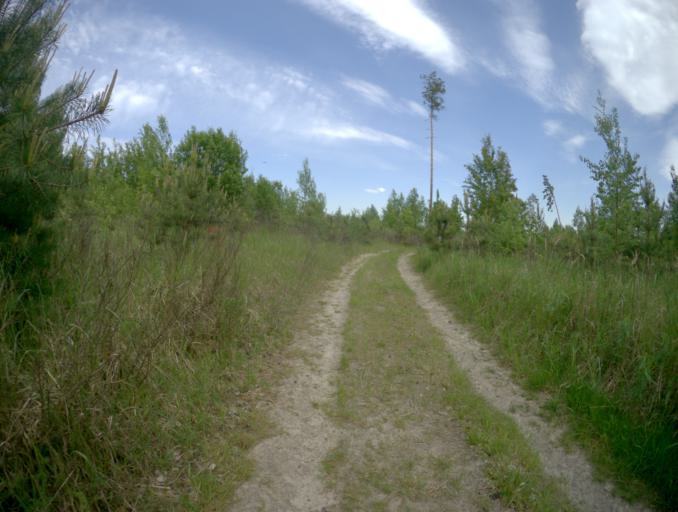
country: RU
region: Vladimir
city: Ivanishchi
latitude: 55.7045
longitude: 40.4660
